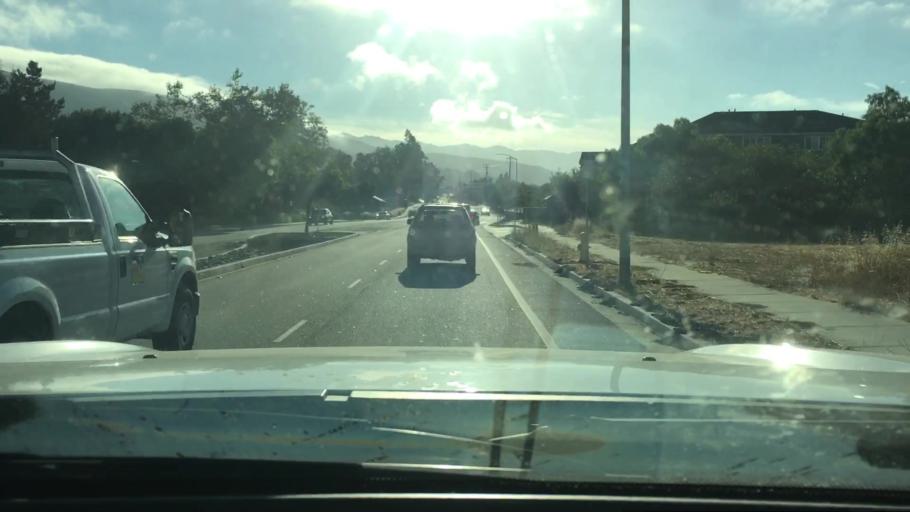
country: US
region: California
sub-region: San Luis Obispo County
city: San Luis Obispo
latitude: 35.2613
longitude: -120.6478
